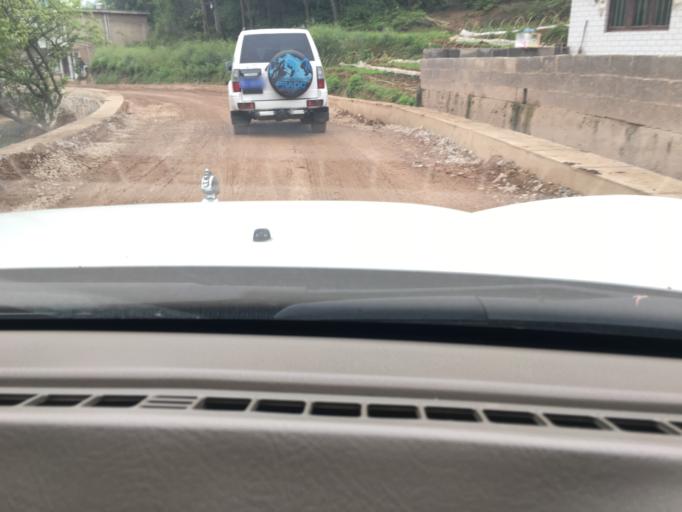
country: CN
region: Guizhou Sheng
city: Supu
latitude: 26.7331
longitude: 106.4371
